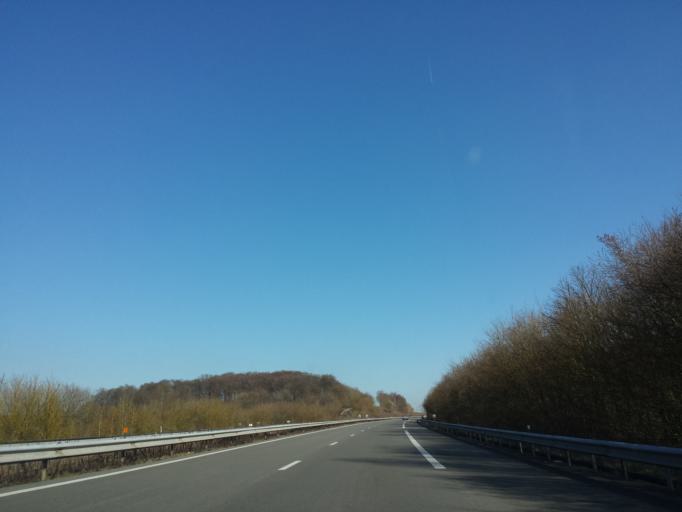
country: FR
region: Picardie
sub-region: Departement de la Somme
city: Conty
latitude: 49.6773
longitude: 2.2126
